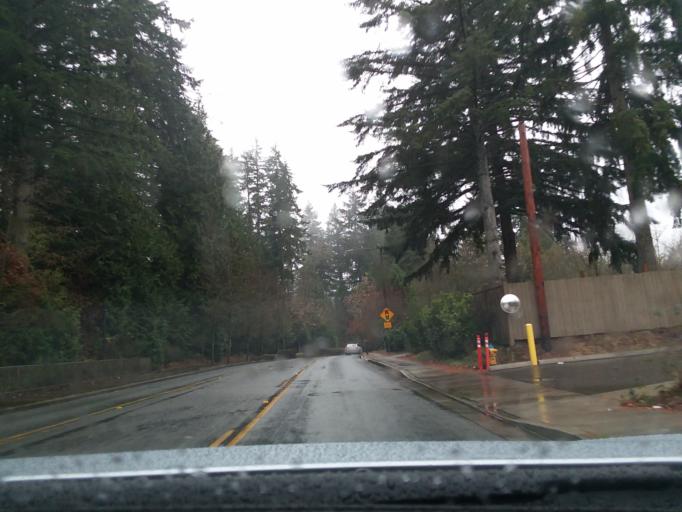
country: US
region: Washington
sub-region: Snohomish County
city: Mill Creek
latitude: 47.8748
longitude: -122.2162
